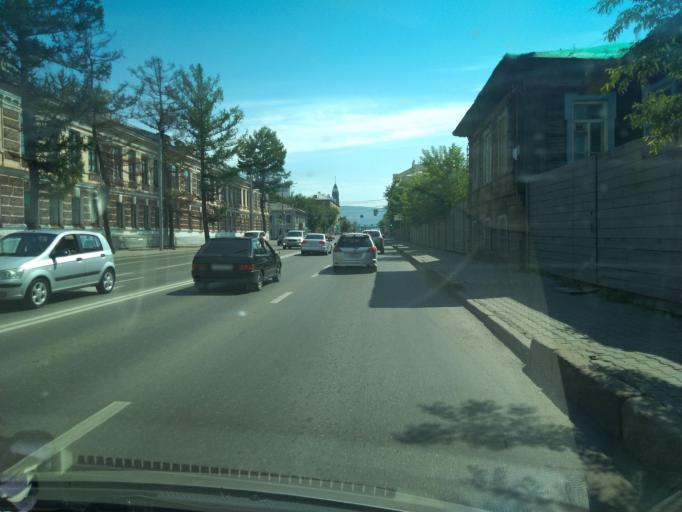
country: RU
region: Krasnoyarskiy
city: Krasnoyarsk
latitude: 56.0145
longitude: 92.8708
